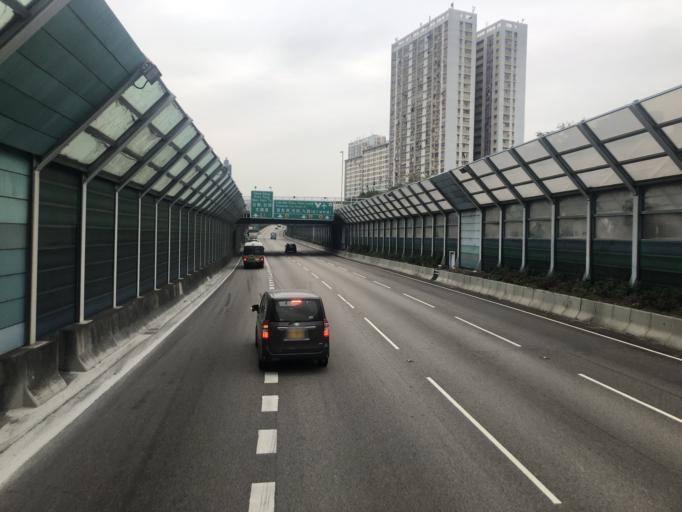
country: HK
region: Tai Po
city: Tai Po
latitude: 22.4987
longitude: 114.1284
